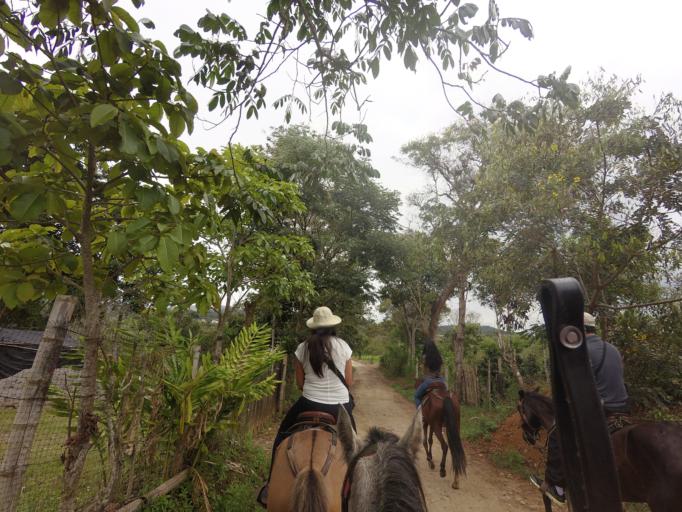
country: CO
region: Huila
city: San Agustin
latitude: 1.8905
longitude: -76.2942
